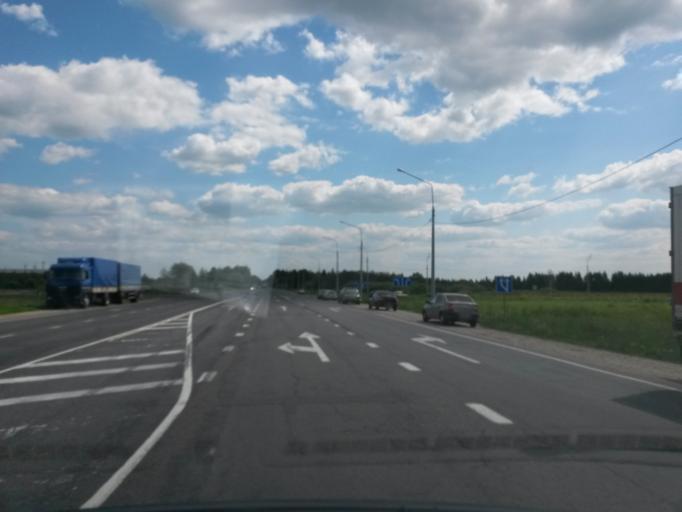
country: RU
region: Jaroslavl
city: Yaroslavl
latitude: 57.5511
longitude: 39.8885
